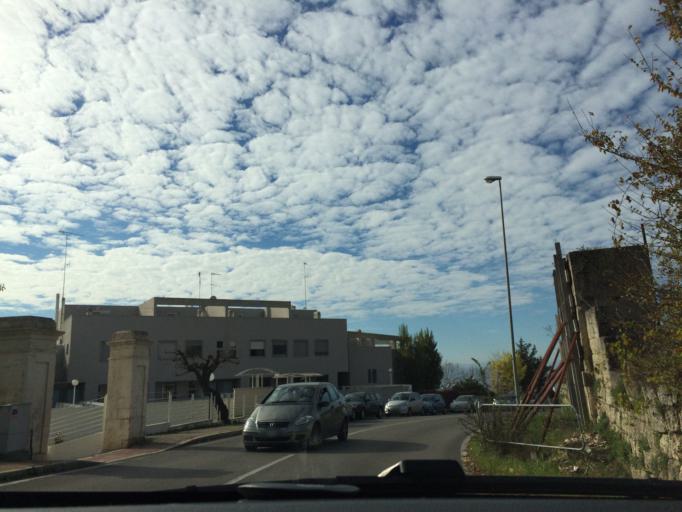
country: IT
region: Basilicate
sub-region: Provincia di Matera
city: Matera
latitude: 40.6557
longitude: 16.6161
